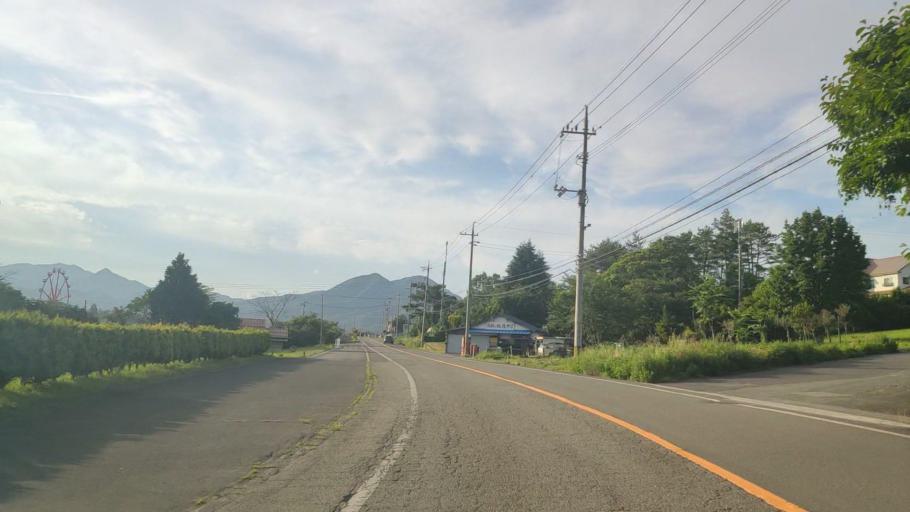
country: JP
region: Tottori
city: Kurayoshi
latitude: 35.2872
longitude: 133.6375
